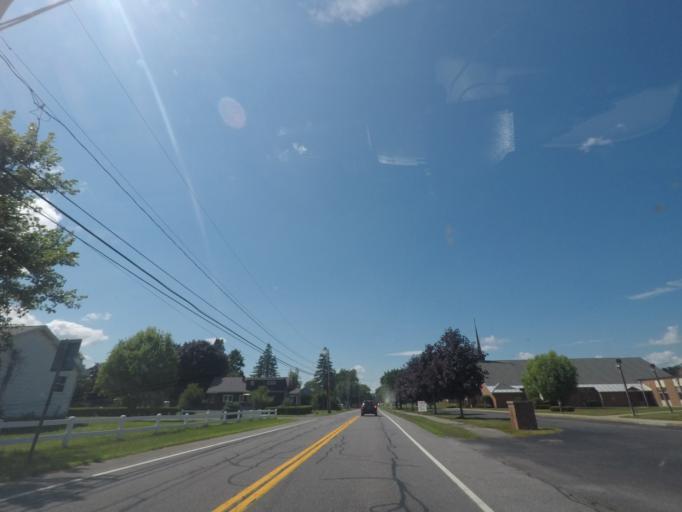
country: US
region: New York
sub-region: Schenectady County
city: Rotterdam
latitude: 42.7938
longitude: -73.9872
